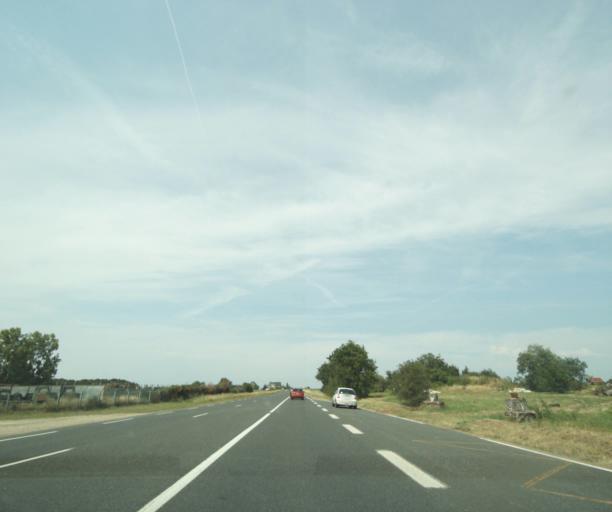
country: FR
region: Centre
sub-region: Departement d'Indre-et-Loire
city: Sorigny
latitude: 47.1911
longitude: 0.6654
